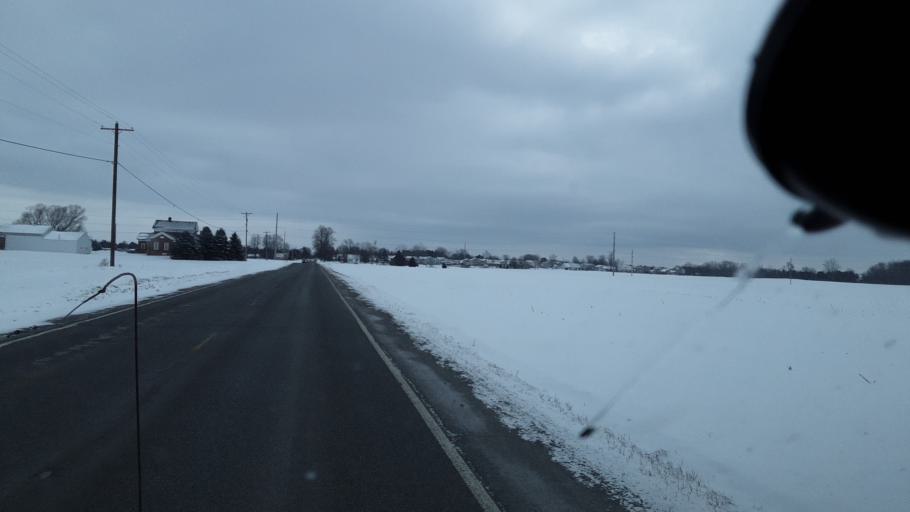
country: US
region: Michigan
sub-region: Ingham County
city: Mason
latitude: 42.5822
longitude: -84.4776
